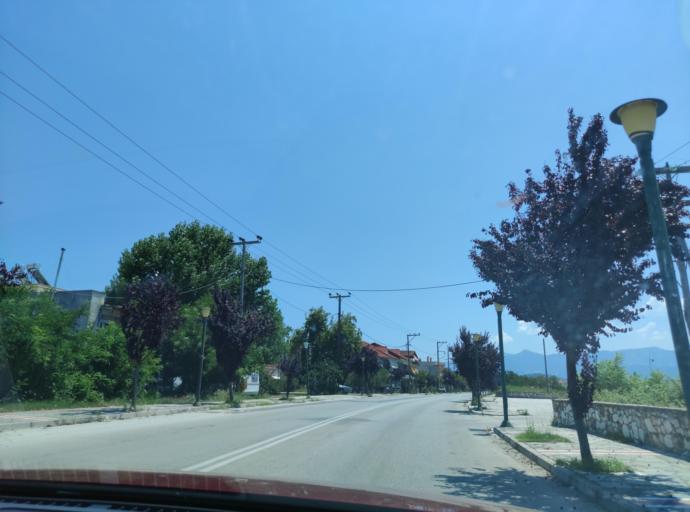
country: GR
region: East Macedonia and Thrace
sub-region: Nomos Kavalas
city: Keramoti
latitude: 40.8643
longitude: 24.7057
